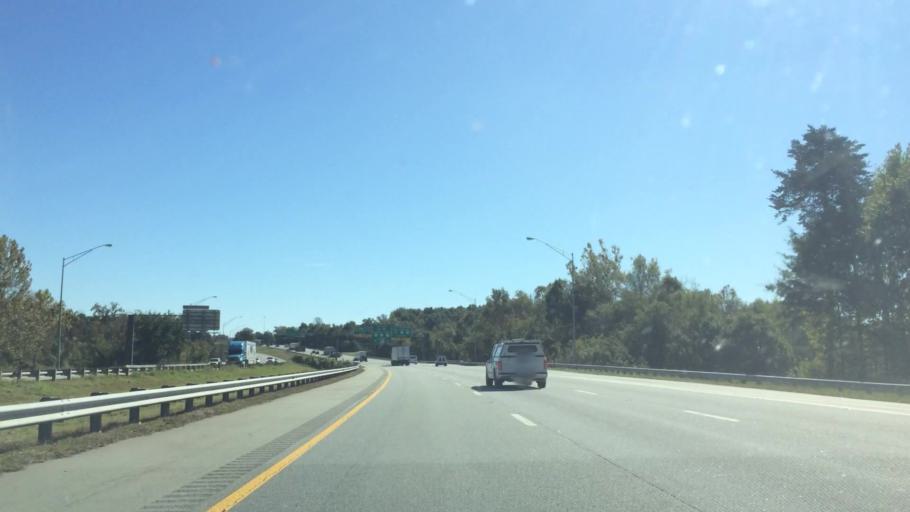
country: US
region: North Carolina
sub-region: Guilford County
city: Greensboro
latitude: 36.0333
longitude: -79.8158
